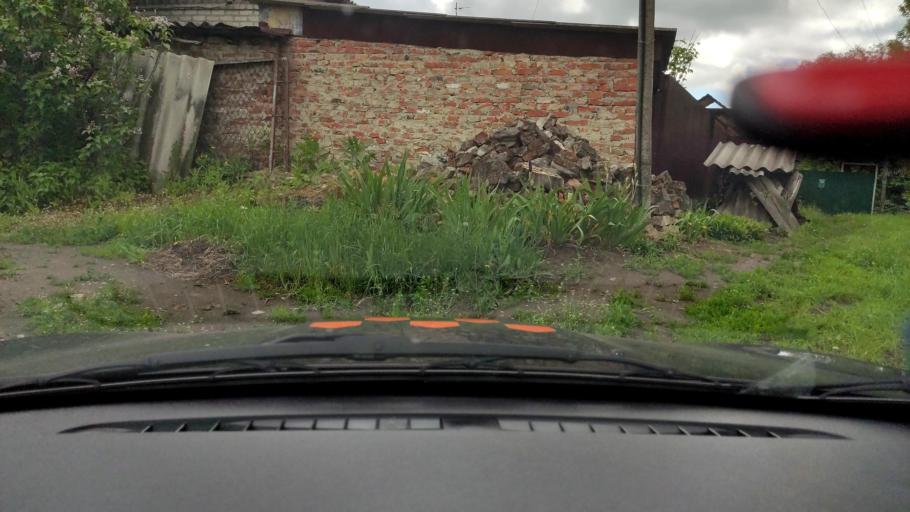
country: RU
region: Voronezj
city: Uryv-Pokrovka
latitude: 51.1056
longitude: 39.1569
